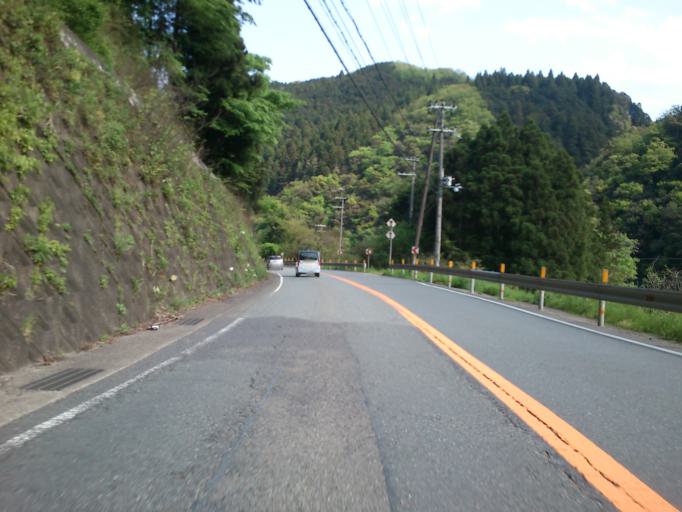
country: JP
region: Kyoto
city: Fukuchiyama
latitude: 35.3207
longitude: 134.9836
